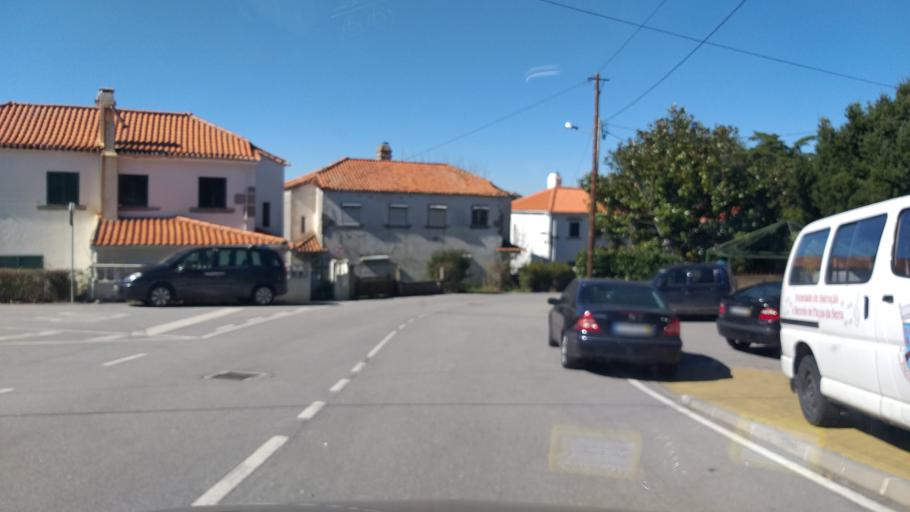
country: PT
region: Guarda
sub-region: Manteigas
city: Manteigas
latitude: 40.4893
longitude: -7.5921
